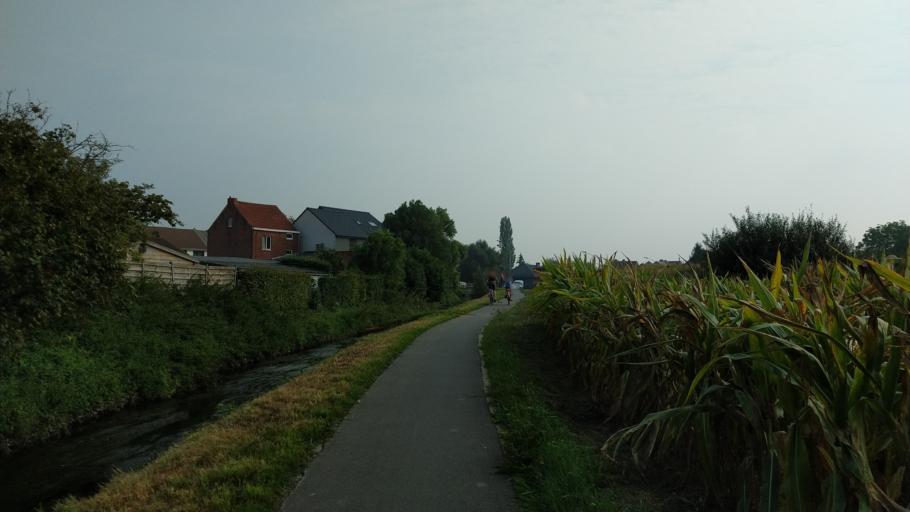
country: BE
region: Flanders
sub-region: Provincie Vlaams-Brabant
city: Rotselaar
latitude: 50.9156
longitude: 4.7150
